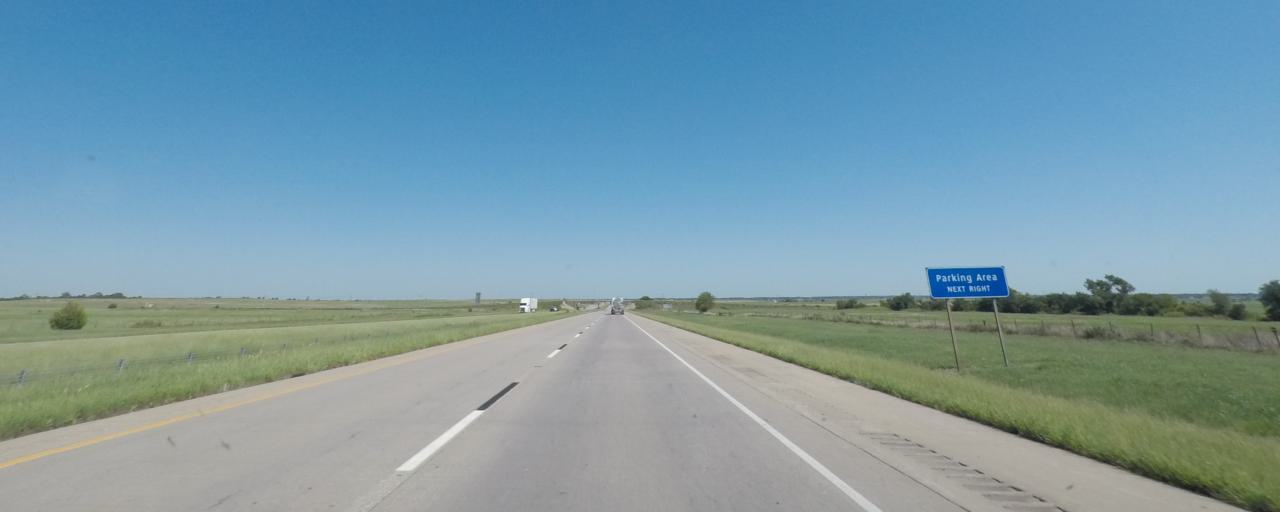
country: US
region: Oklahoma
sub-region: Kay County
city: Tonkawa
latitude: 36.6034
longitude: -97.3456
